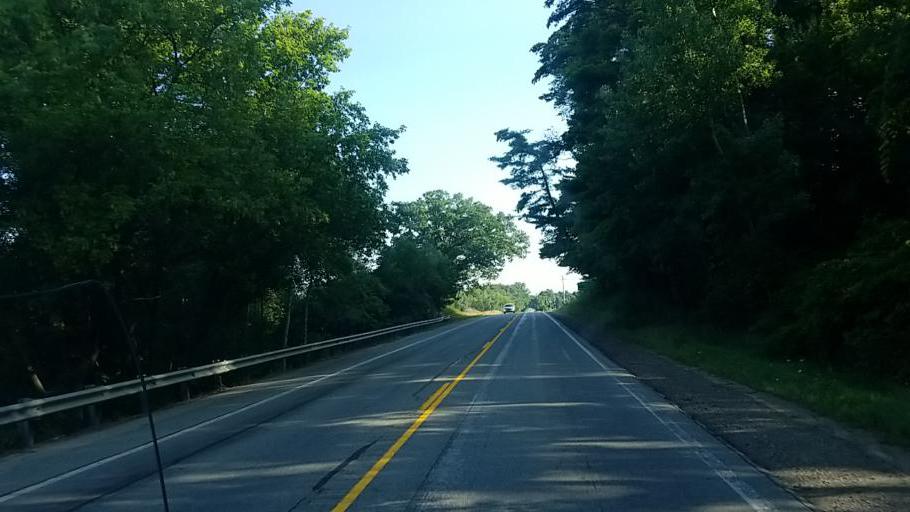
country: US
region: Michigan
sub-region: Newaygo County
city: Fremont
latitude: 43.4785
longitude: -86.0395
